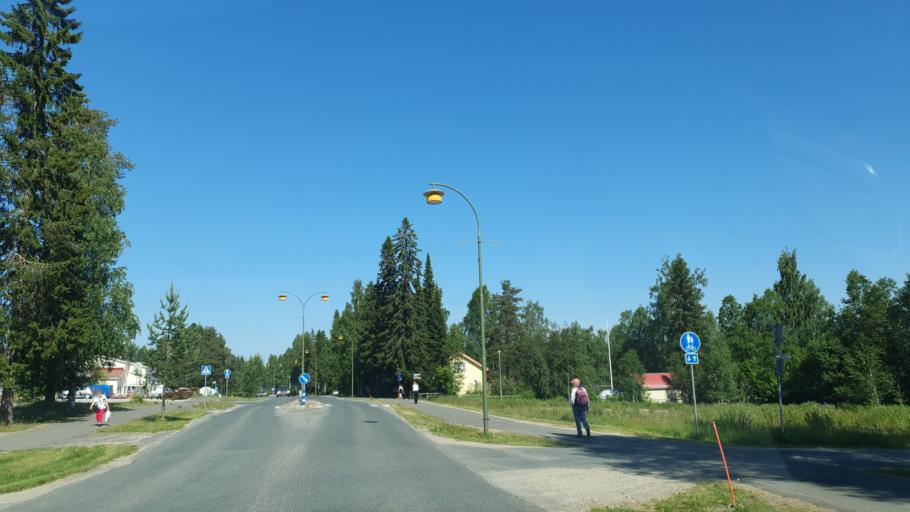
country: FI
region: Lapland
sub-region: Rovaniemi
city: Ranua
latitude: 65.9286
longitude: 26.5180
